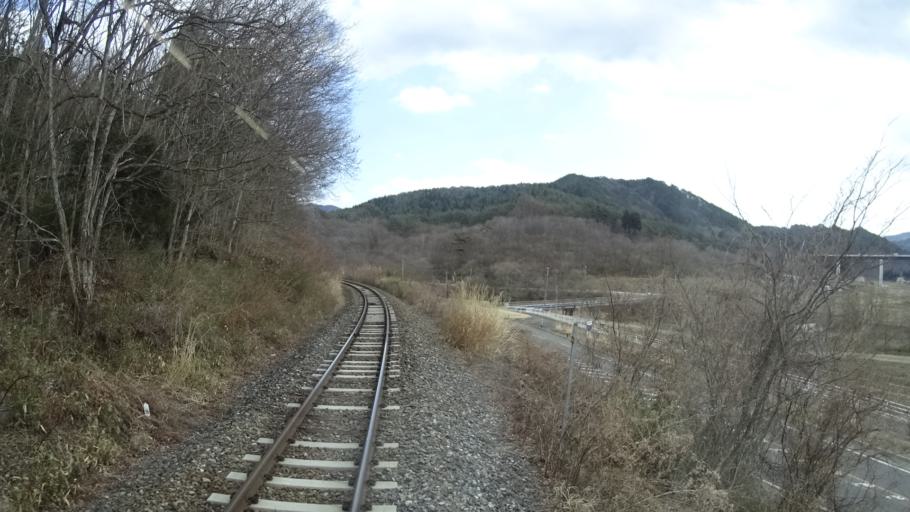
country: JP
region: Iwate
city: Tono
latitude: 39.3021
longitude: 141.3823
